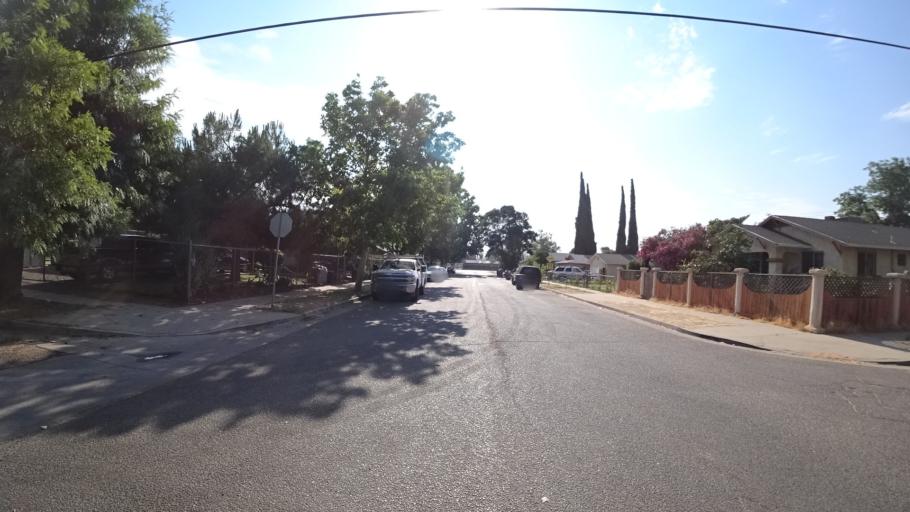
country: US
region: California
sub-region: Fresno County
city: Fresno
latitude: 36.7369
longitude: -119.8100
